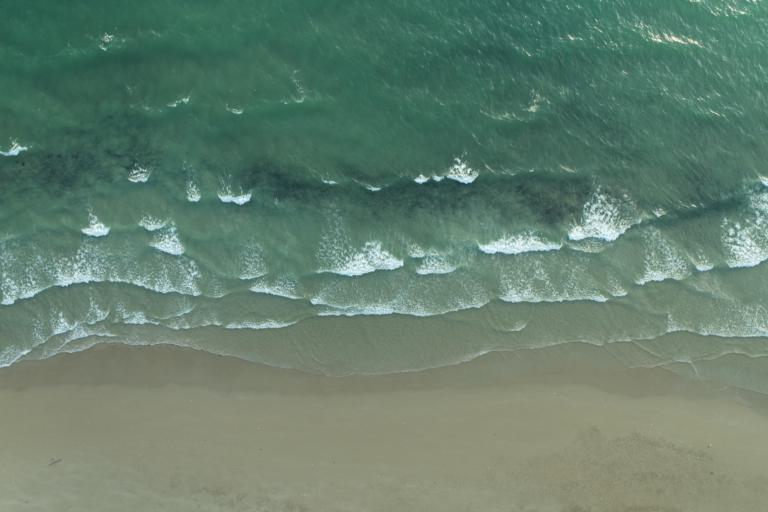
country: TH
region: Rayong
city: Rayong
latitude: 12.6071
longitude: 101.3909
